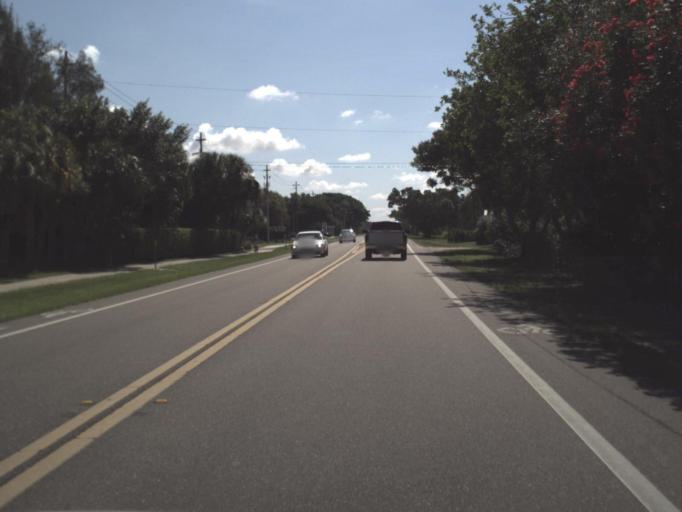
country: US
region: Florida
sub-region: Sarasota County
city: Siesta Key
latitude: 27.3390
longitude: -82.5933
